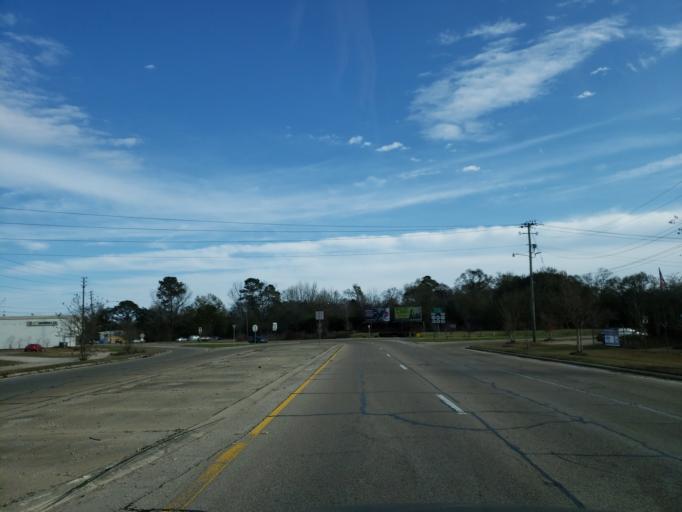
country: US
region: Mississippi
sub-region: Forrest County
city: Hattiesburg
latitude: 31.3410
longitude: -89.2879
